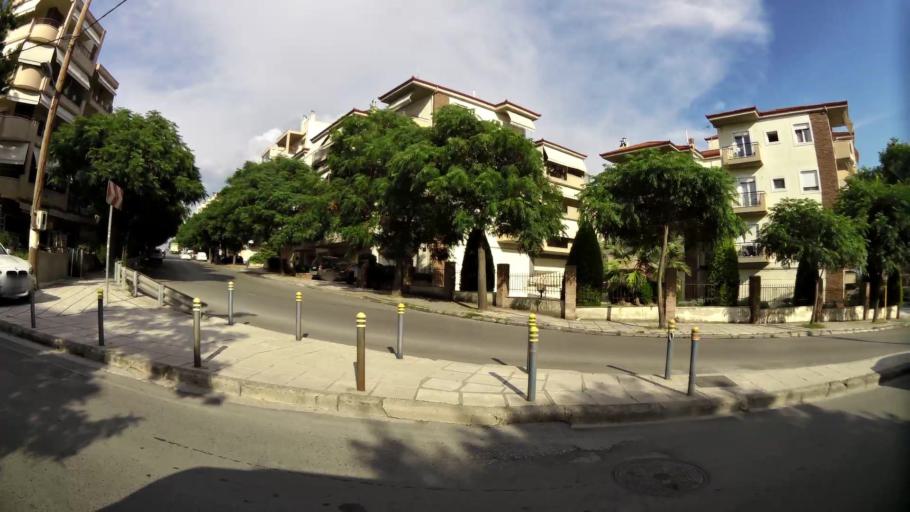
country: GR
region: Central Macedonia
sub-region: Nomos Thessalonikis
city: Kalamaria
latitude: 40.5744
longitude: 22.9628
